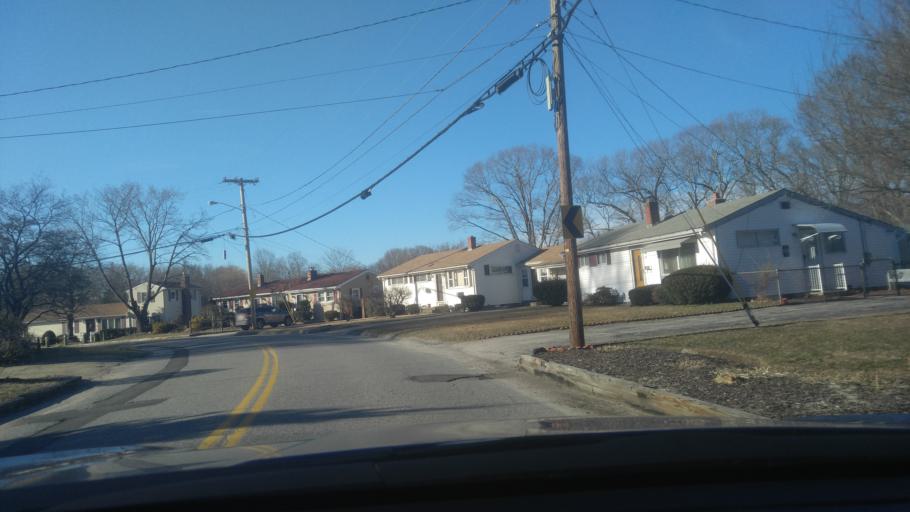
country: US
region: Rhode Island
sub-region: Kent County
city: Warwick
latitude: 41.6974
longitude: -71.4215
